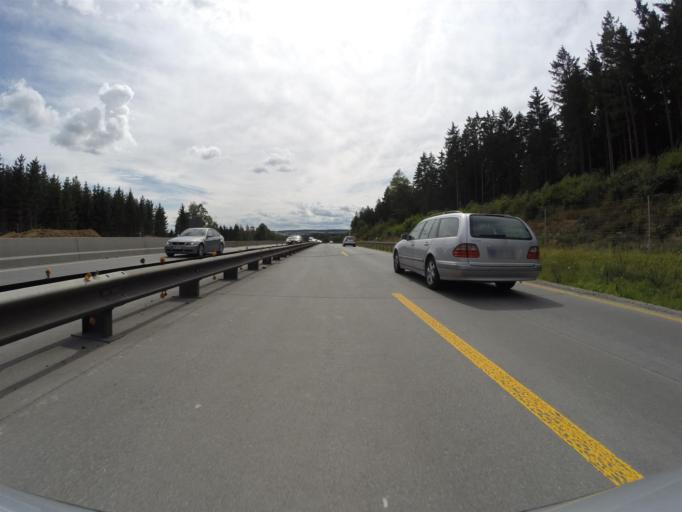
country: DE
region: Thuringia
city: Lemnitz
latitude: 50.7032
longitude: 11.8464
